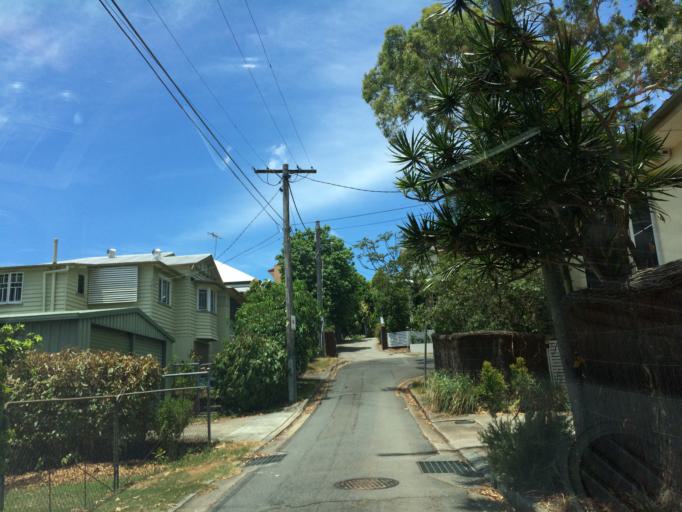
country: AU
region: Queensland
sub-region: Brisbane
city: Milton
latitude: -27.4843
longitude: 153.0040
